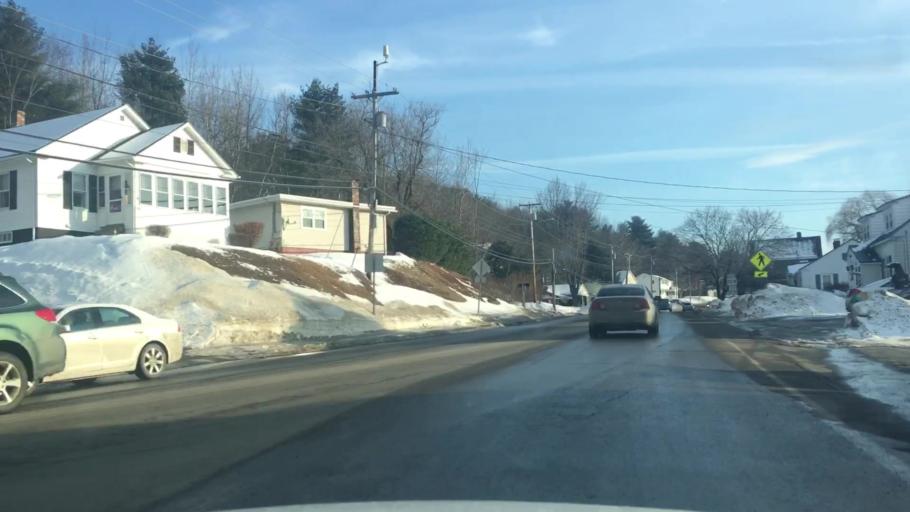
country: US
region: Maine
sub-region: Kennebec County
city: Augusta
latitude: 44.3341
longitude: -69.7779
